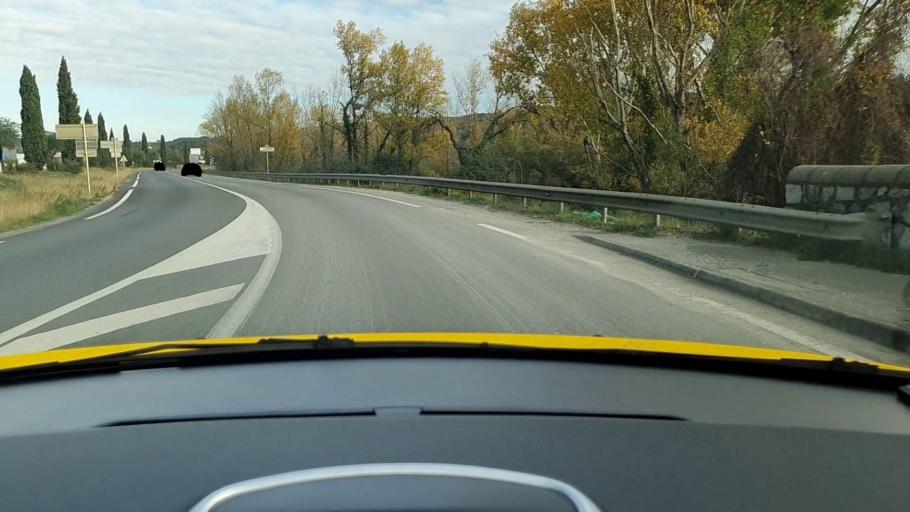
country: FR
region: Languedoc-Roussillon
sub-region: Departement du Gard
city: Saint-Martin-de-Valgalgues
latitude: 44.1570
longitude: 4.0848
